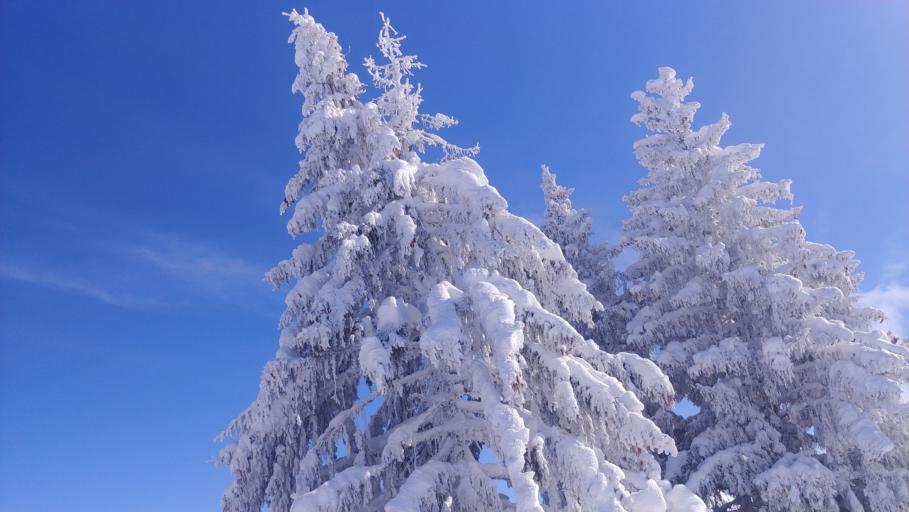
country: FR
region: Rhone-Alpes
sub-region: Departement de la Haute-Savoie
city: Morzine
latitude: 46.1667
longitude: 6.6924
